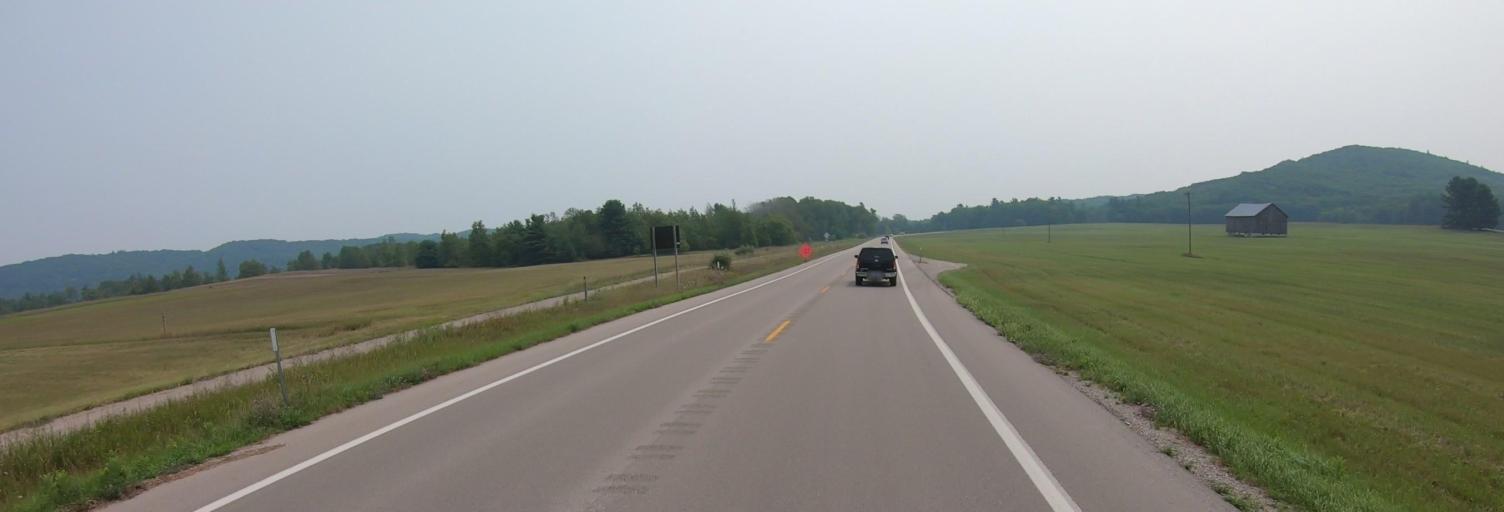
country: US
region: Michigan
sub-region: Leelanau County
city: Leland
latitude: 44.9377
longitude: -85.9349
